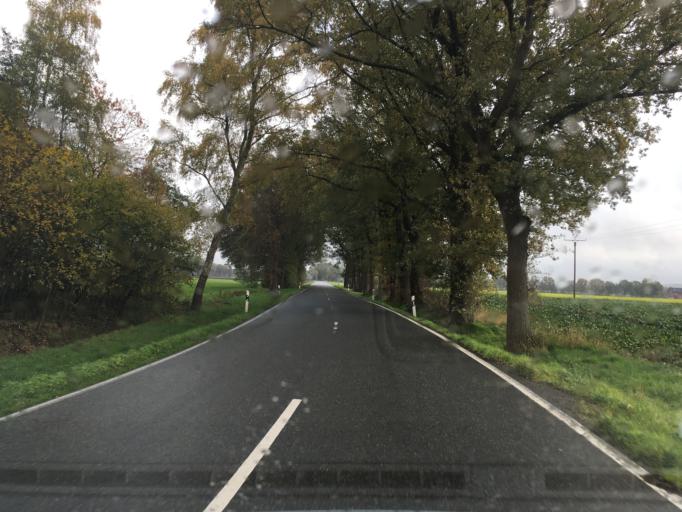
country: DE
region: North Rhine-Westphalia
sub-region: Regierungsbezirk Munster
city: Velen
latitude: 51.8715
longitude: 7.0223
